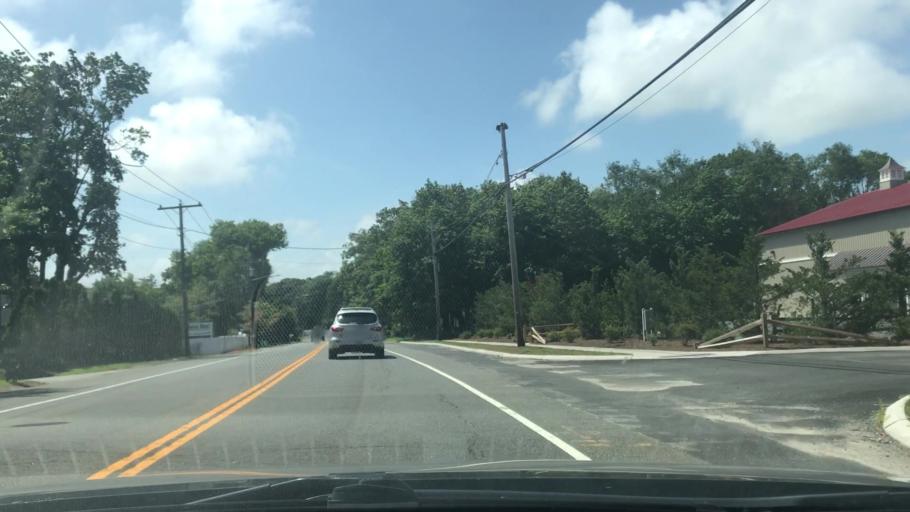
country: US
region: New York
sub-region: Suffolk County
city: Riverhead
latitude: 40.9170
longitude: -72.6920
